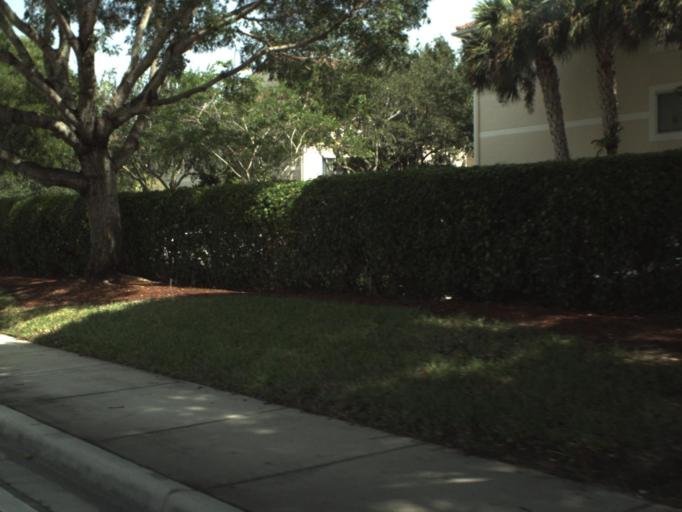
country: US
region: Florida
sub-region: Broward County
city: Coral Springs
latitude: 26.2728
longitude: -80.2882
